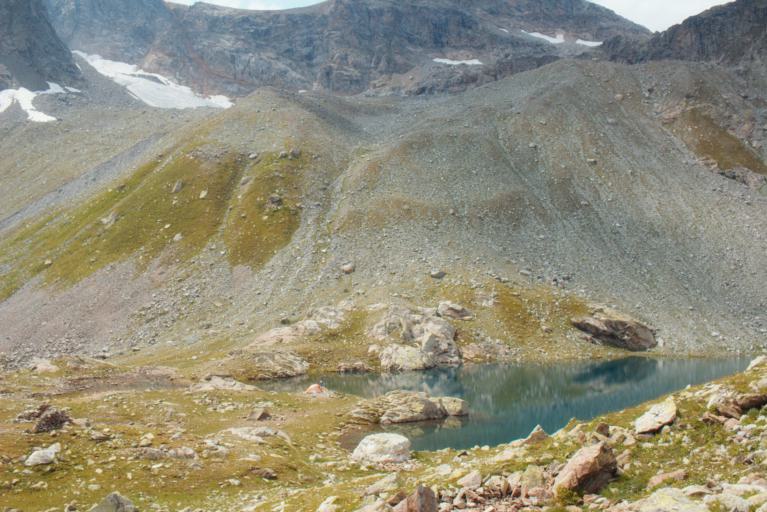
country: RU
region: Karachayevo-Cherkesiya
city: Nizhniy Arkhyz
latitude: 43.4518
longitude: 41.2310
